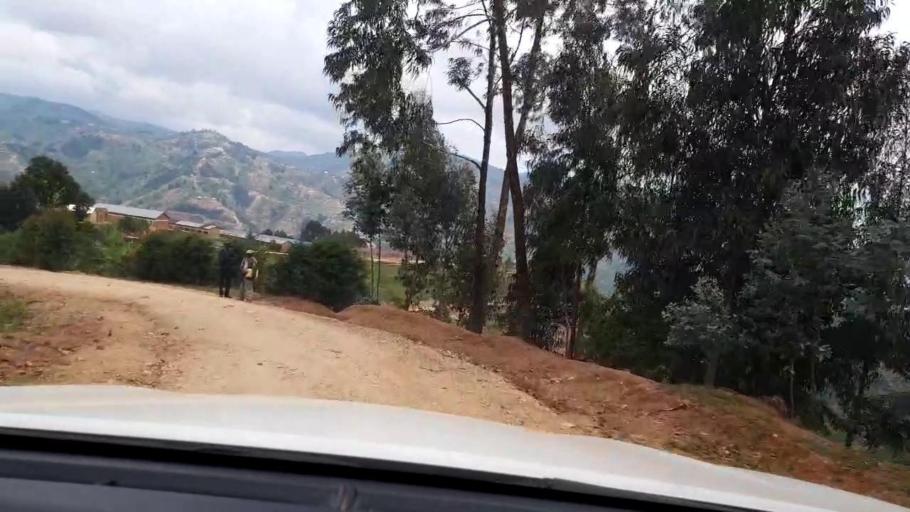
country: RW
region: Western Province
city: Kibuye
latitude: -1.8307
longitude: 29.5454
